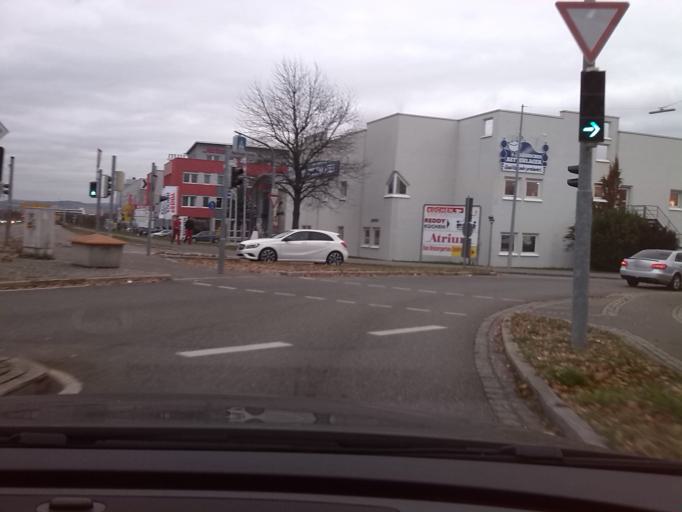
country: DE
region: Baden-Wuerttemberg
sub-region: Regierungsbezirk Stuttgart
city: Fellbach
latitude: 48.8154
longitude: 9.2813
